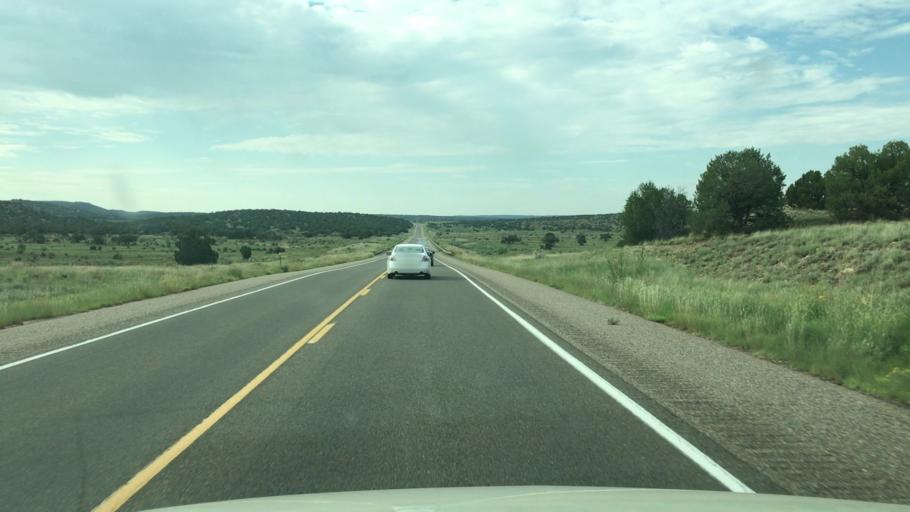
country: US
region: New Mexico
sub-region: Santa Fe County
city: Eldorado at Santa Fe
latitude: 35.3107
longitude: -105.8296
